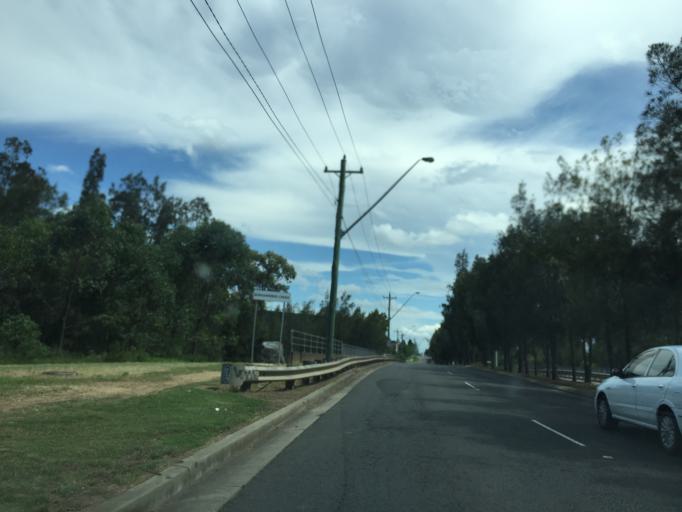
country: AU
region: New South Wales
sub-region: Blacktown
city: Doonside
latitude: -33.7826
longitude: 150.8728
